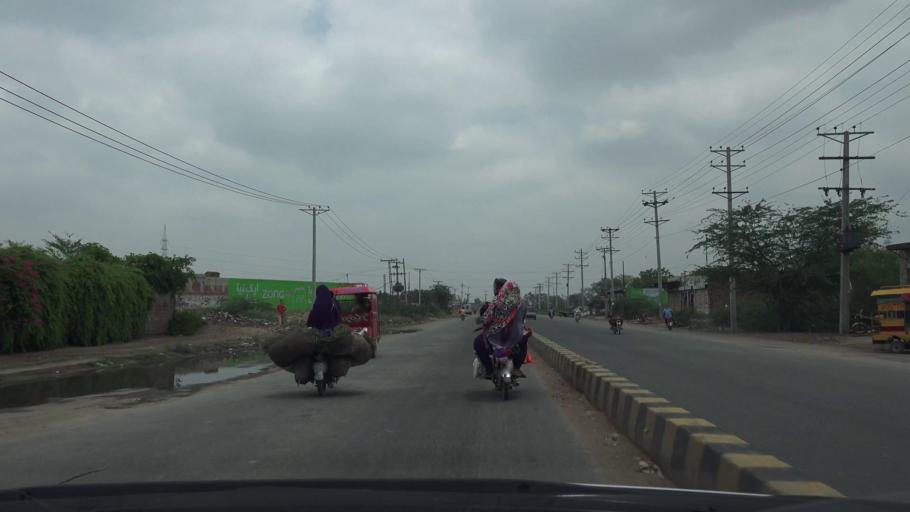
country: PK
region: Punjab
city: Faisalabad
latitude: 31.3922
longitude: 73.1856
